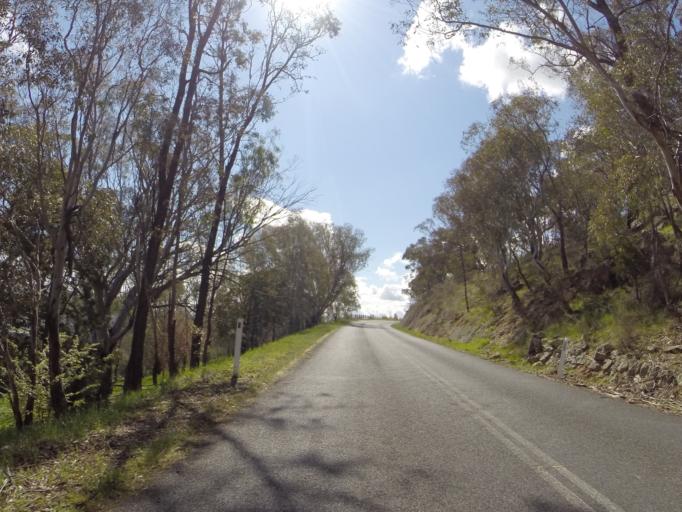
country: AU
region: New South Wales
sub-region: Yass Valley
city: Yass
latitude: -34.9893
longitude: 148.8411
